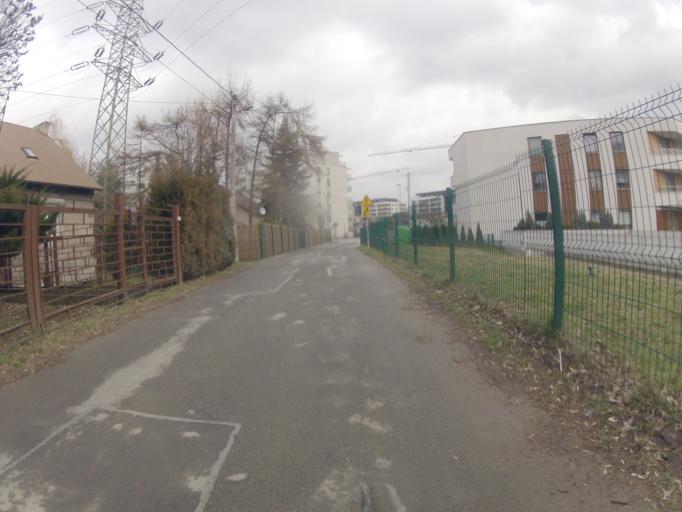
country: PL
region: Lesser Poland Voivodeship
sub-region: Krakow
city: Krakow
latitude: 50.0669
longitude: 19.9838
